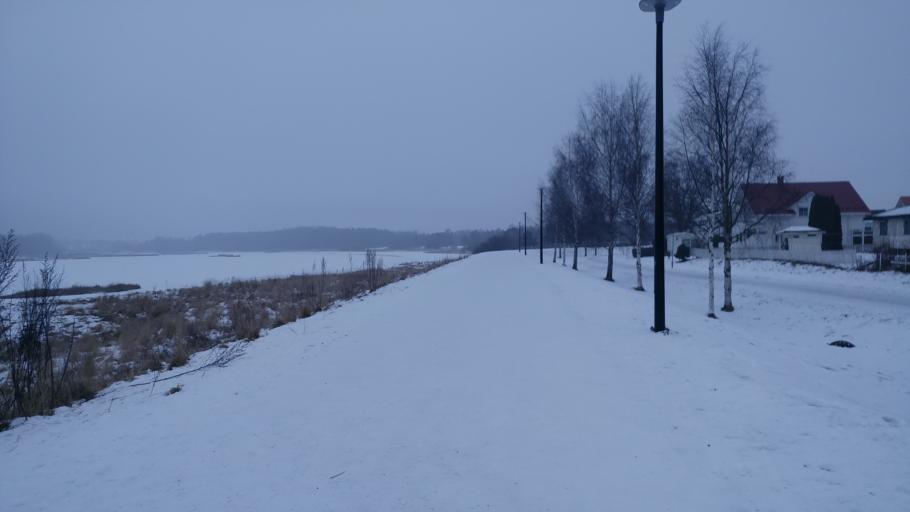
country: NO
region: Akershus
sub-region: Skedsmo
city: Lillestrom
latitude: 59.9609
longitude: 11.0291
